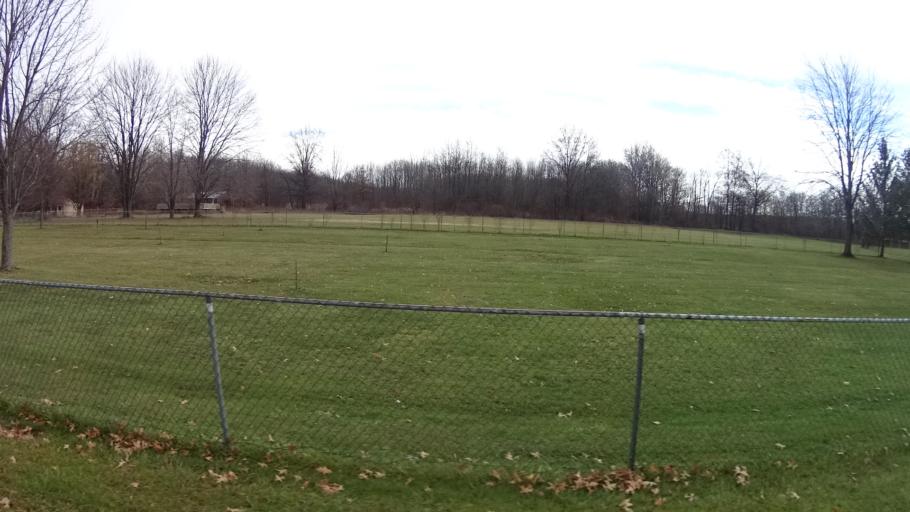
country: US
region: Ohio
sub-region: Lorain County
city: North Ridgeville
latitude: 41.3697
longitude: -82.0333
